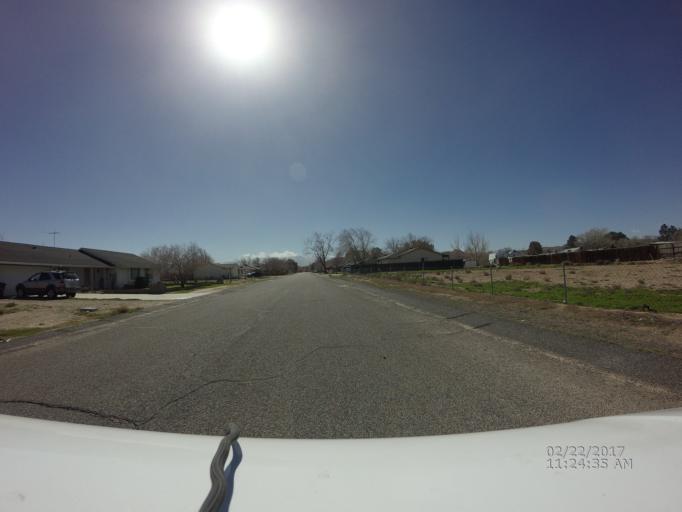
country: US
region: California
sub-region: Los Angeles County
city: Lake Los Angeles
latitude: 34.6225
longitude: -117.8128
